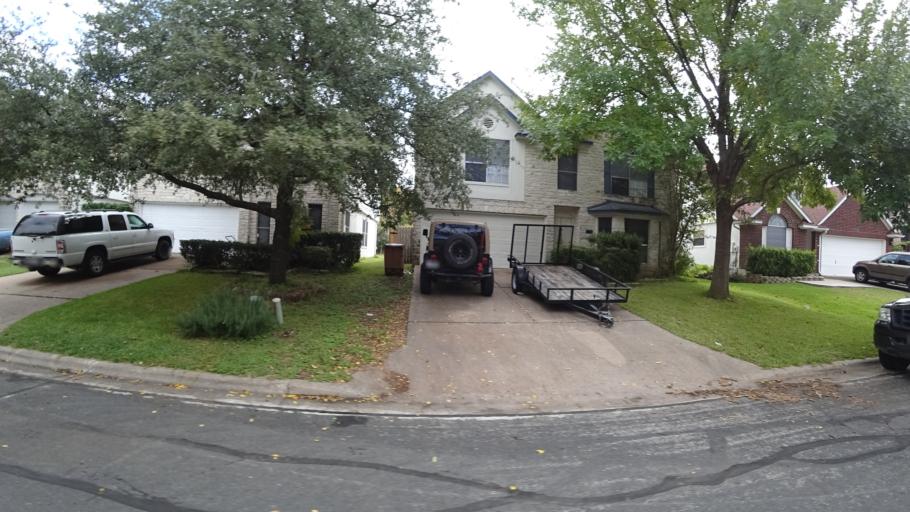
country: US
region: Texas
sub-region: Travis County
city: Shady Hollow
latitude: 30.1928
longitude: -97.8345
